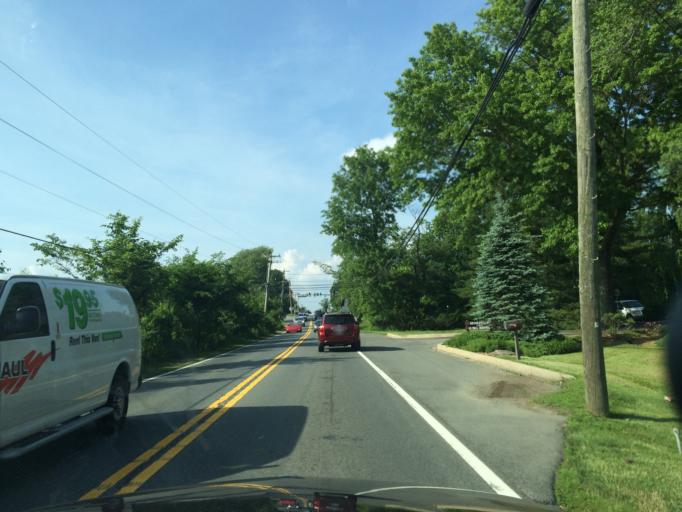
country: US
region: Maryland
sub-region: Montgomery County
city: Olney
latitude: 39.2200
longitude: -77.0603
